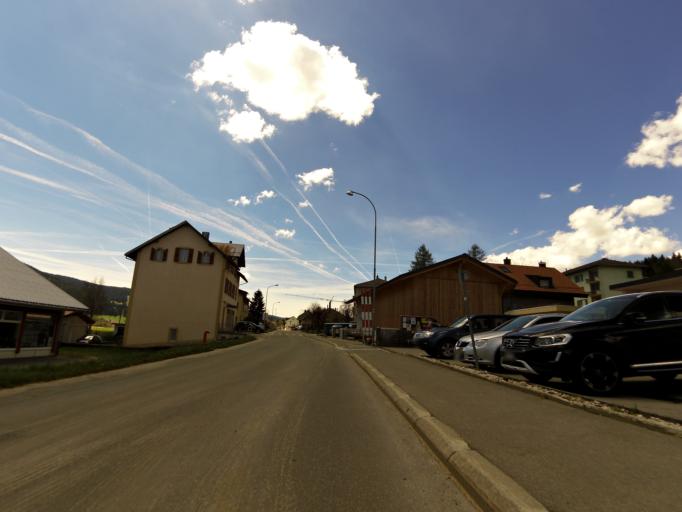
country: CH
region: Vaud
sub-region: Jura-Nord vaudois District
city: Le Chenit
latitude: 46.5985
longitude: 6.2184
